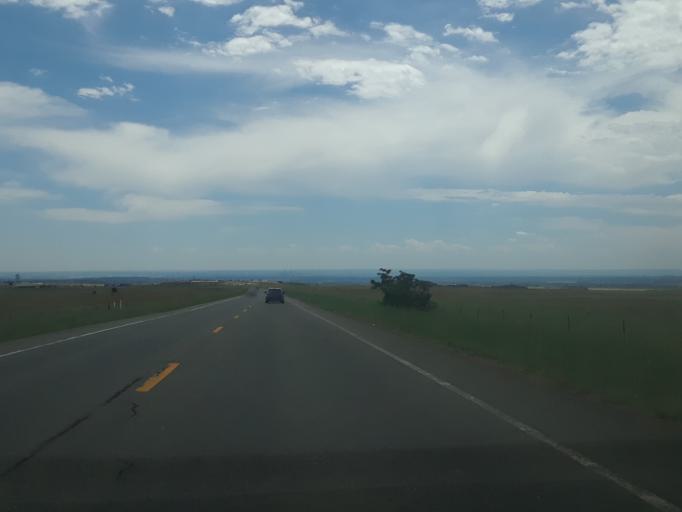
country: US
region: Colorado
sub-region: Jefferson County
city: Golden
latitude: 39.8705
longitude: -105.2587
